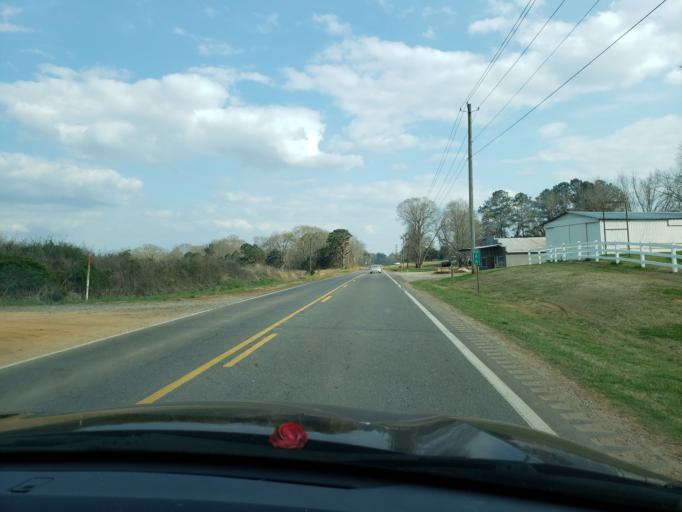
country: US
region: Alabama
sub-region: Hale County
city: Greensboro
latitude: 32.7157
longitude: -87.6181
